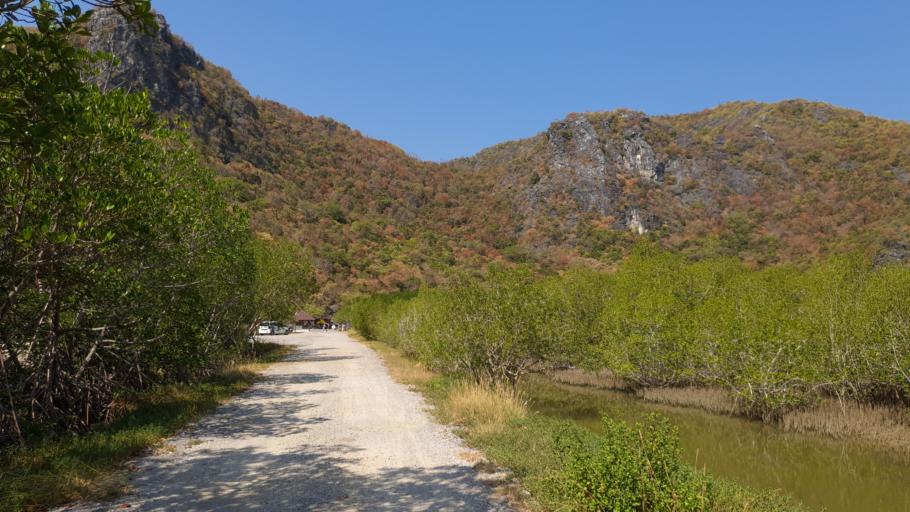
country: TH
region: Prachuap Khiri Khan
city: Sam Roi Yot
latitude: 12.2017
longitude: 99.9930
